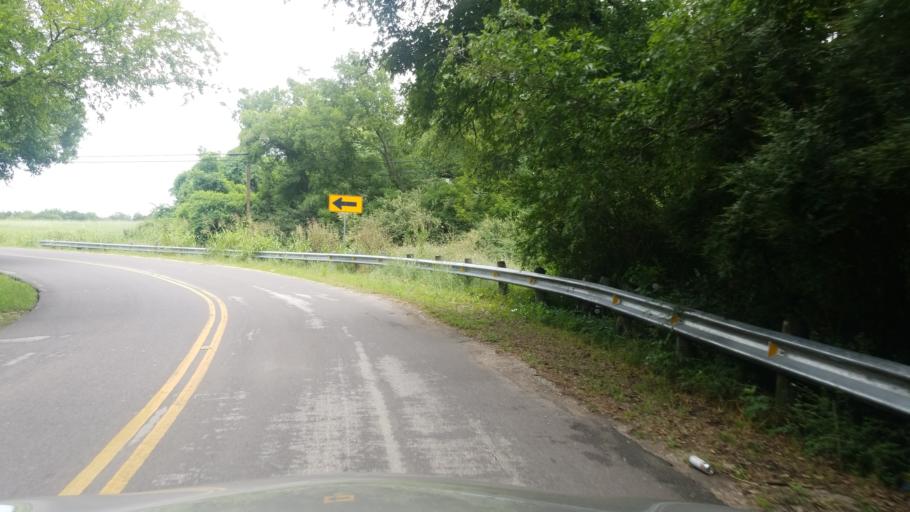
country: US
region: Texas
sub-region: Dallas County
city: Duncanville
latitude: 32.6860
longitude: -96.9341
